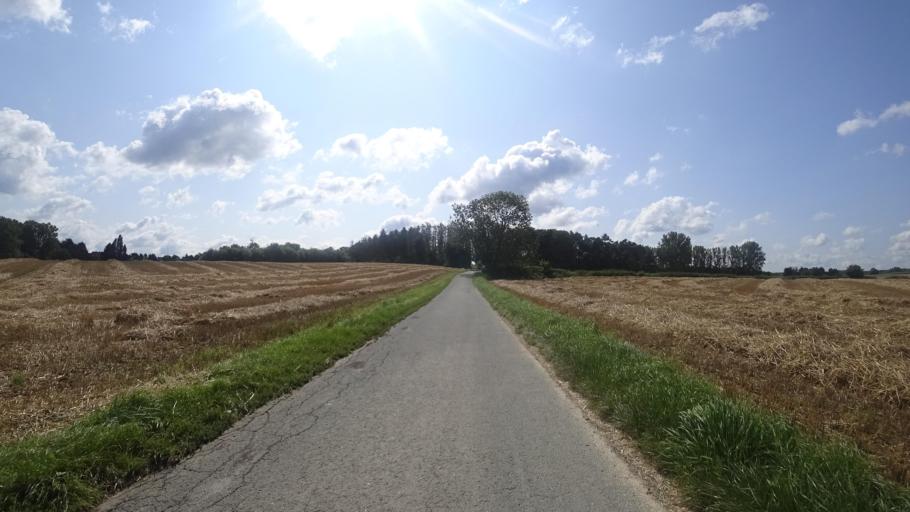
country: BE
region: Flanders
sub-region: Provincie Vlaams-Brabant
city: Tervuren
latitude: 50.8232
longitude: 4.5553
